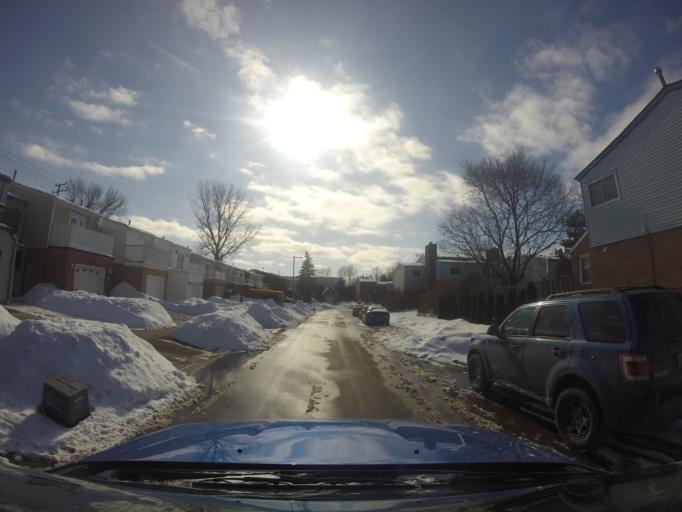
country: CA
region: Ontario
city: Mississauga
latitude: 43.5238
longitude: -79.6169
